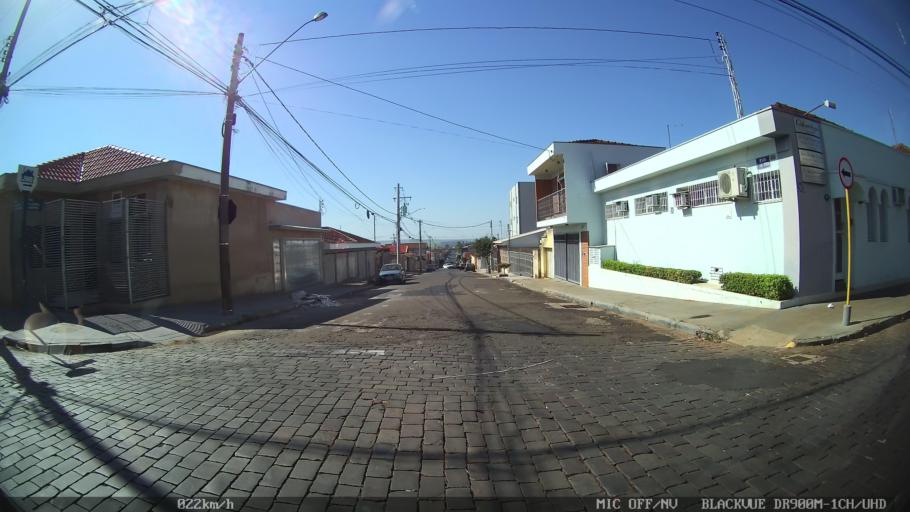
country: BR
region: Sao Paulo
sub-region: Batatais
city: Batatais
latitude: -20.8953
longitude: -47.5837
